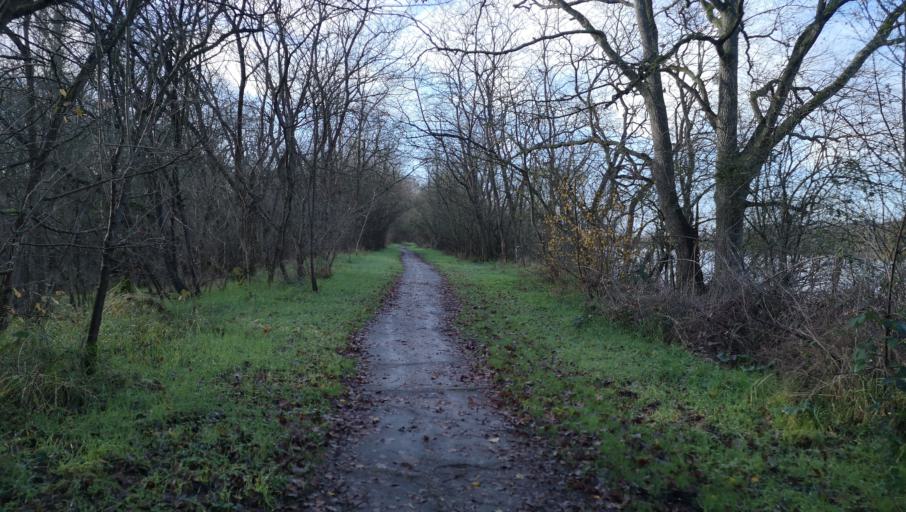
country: FR
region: Centre
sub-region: Departement du Loiret
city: Saint-Hilaire-Saint-Mesmin
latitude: 47.8745
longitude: 1.8283
